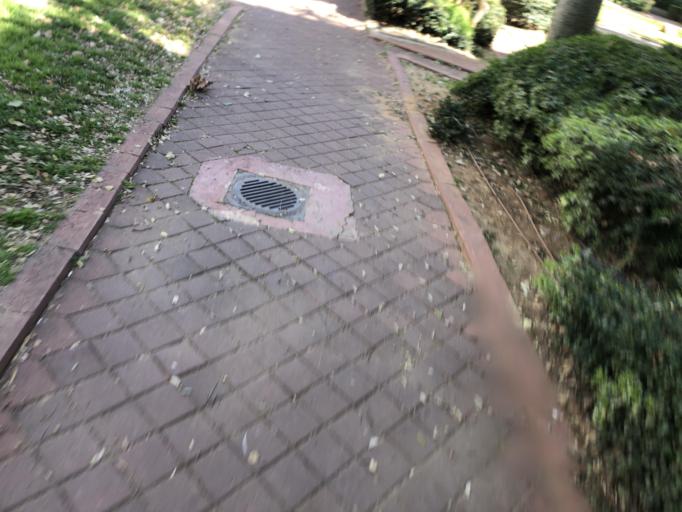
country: IL
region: Tel Aviv
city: Bat Yam
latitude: 32.0074
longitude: 34.7583
